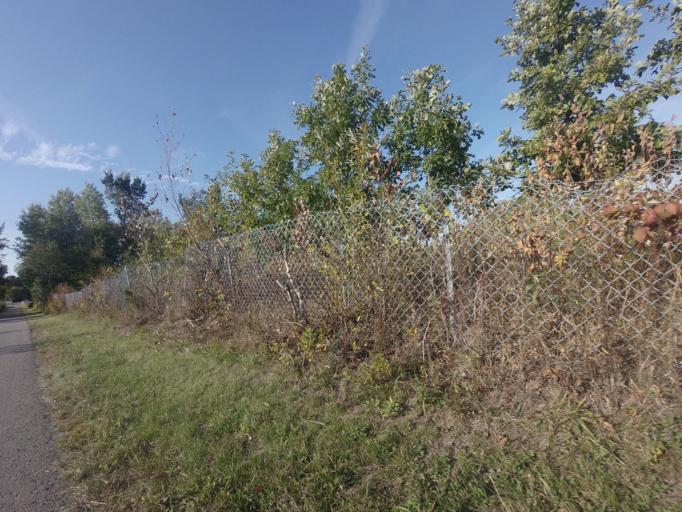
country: CA
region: Quebec
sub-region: Laurentides
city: Saint-Jerome
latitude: 45.7408
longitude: -73.9570
